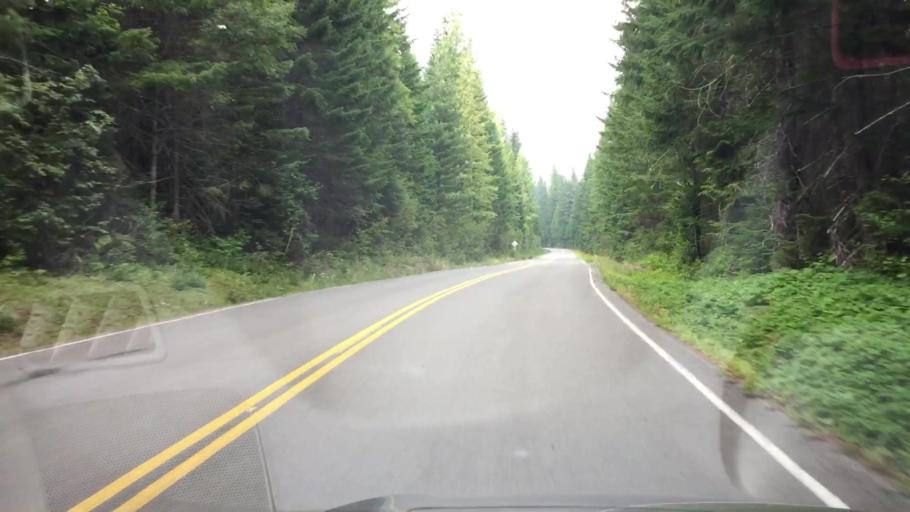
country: US
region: Washington
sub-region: Klickitat County
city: White Salmon
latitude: 46.1248
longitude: -121.6271
